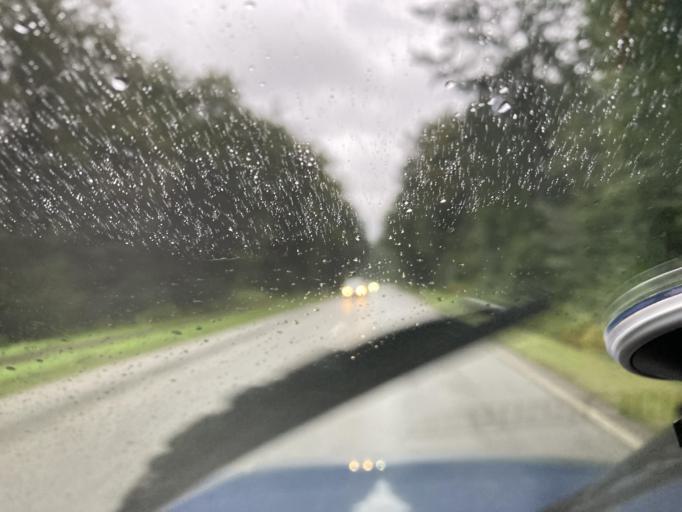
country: DE
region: Schleswig-Holstein
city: Horsten
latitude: 54.2729
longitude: 9.5666
